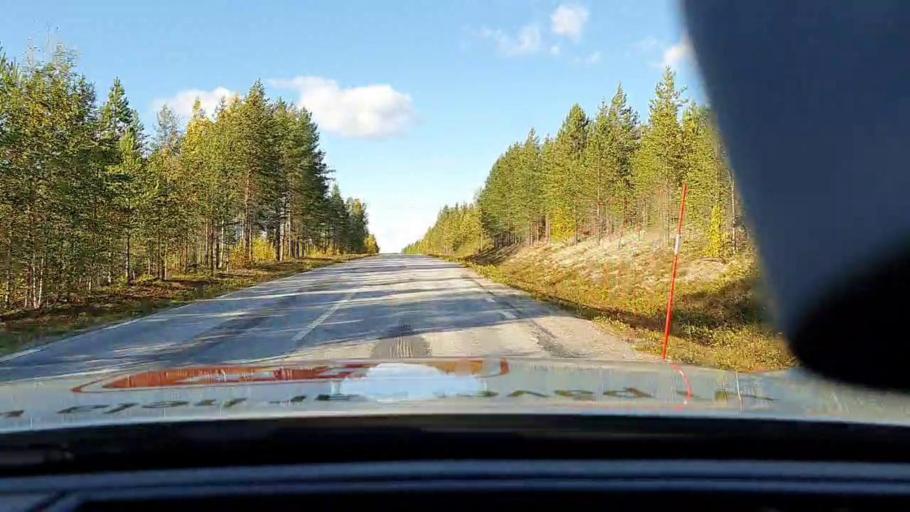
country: SE
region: Norrbotten
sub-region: Pitea Kommun
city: Norrfjarden
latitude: 65.4526
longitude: 21.4565
